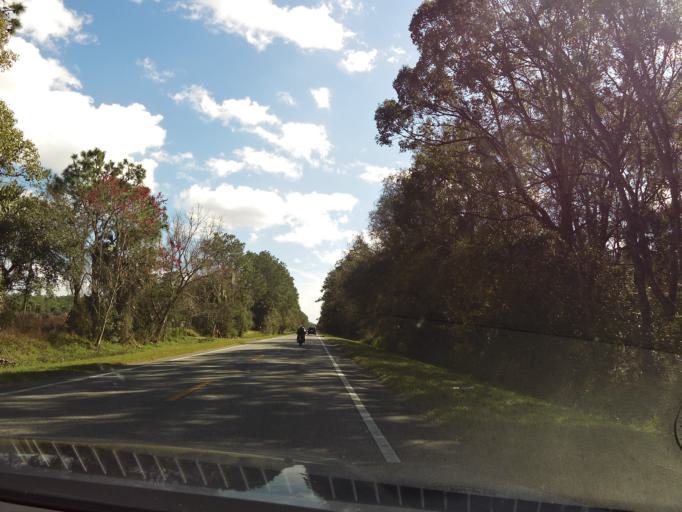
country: US
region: Florida
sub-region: Volusia County
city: De Leon Springs
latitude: 29.1488
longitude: -81.3721
